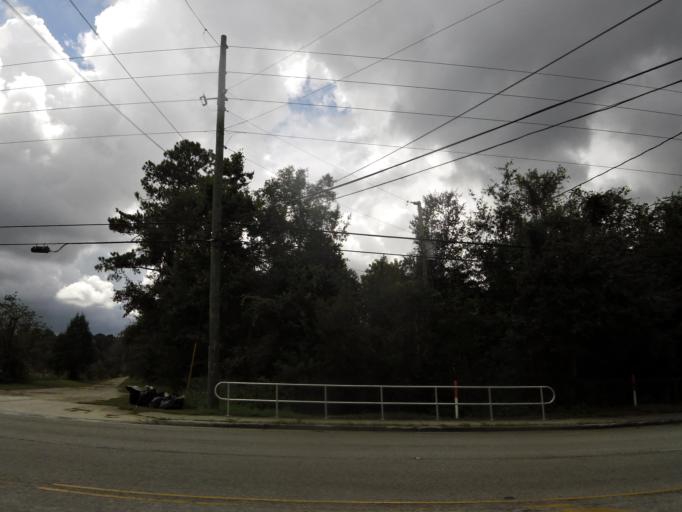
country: US
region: Florida
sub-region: Clay County
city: Lakeside
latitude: 30.1035
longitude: -81.7887
